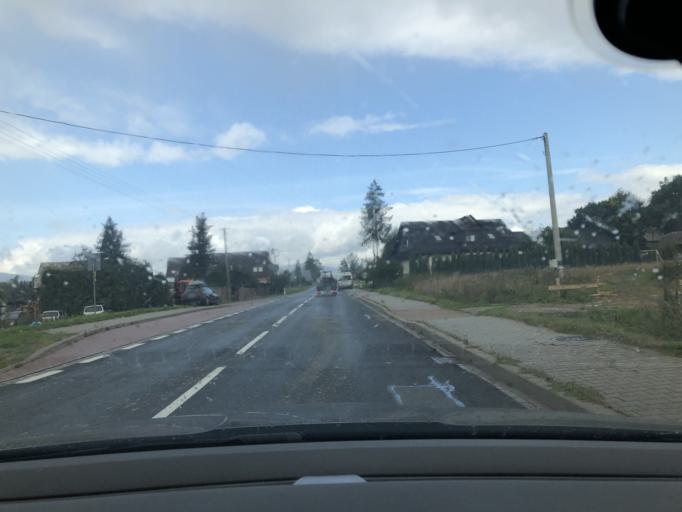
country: PL
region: Lesser Poland Voivodeship
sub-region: Powiat nowotarski
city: Zubrzyca Dolna
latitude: 49.5105
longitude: 19.6753
